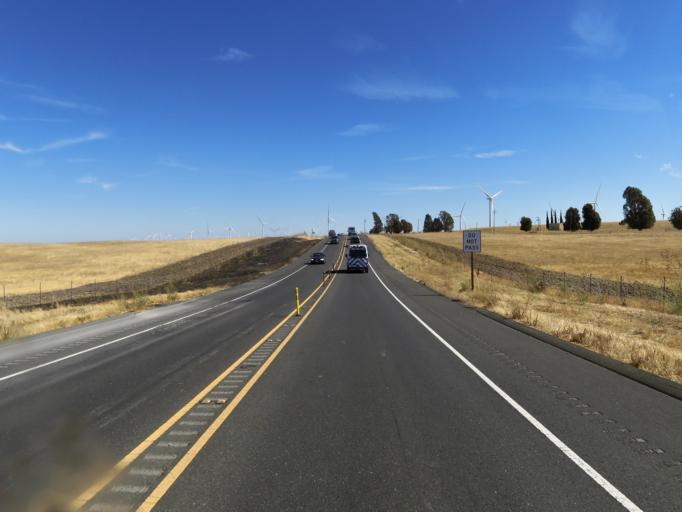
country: US
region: California
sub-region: Solano County
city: Rio Vista
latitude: 38.1856
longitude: -121.8472
